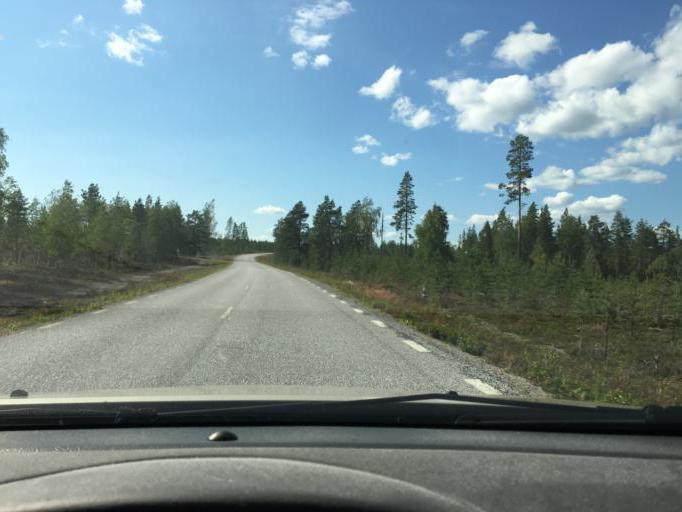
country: SE
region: Norrbotten
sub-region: Kalix Kommun
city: Toere
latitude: 66.0527
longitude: 22.4829
